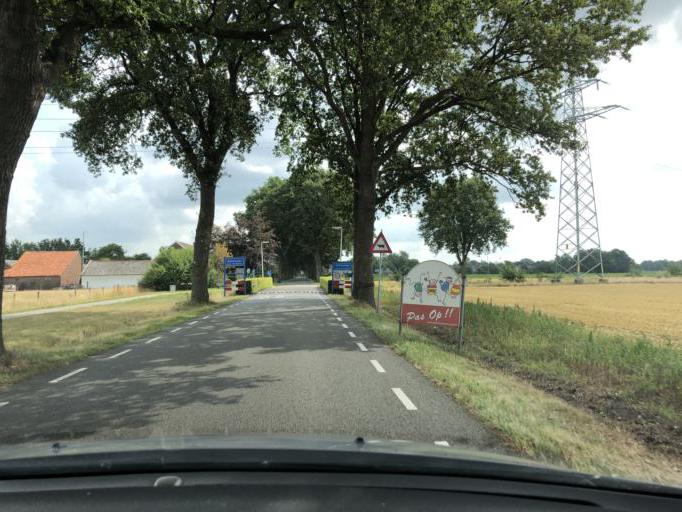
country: NL
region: Drenthe
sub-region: Gemeente Hoogeveen
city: Hoogeveen
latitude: 52.6739
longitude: 6.4799
